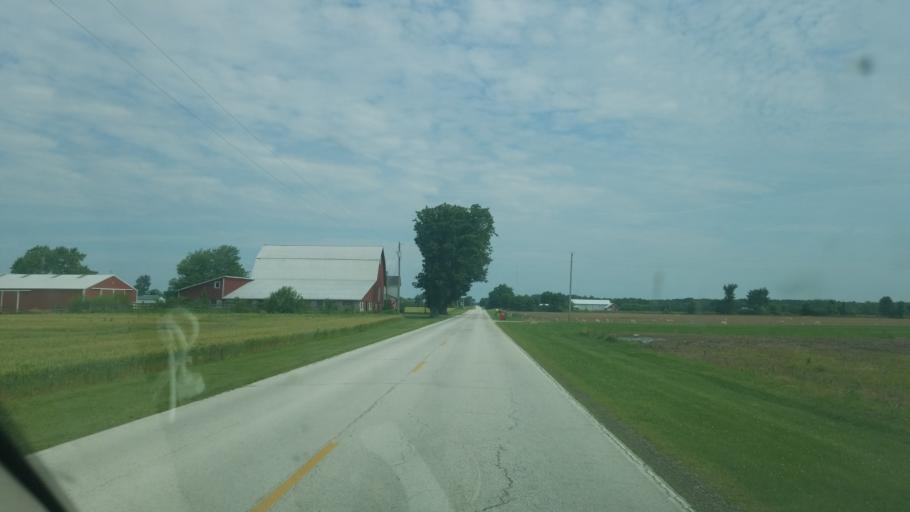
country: US
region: Ohio
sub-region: Seneca County
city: Fostoria
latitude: 41.0873
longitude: -83.4784
